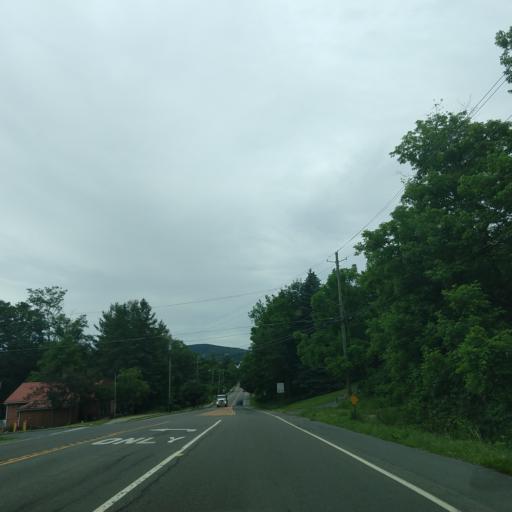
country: US
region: New York
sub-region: Tompkins County
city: Dryden
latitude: 42.4900
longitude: -76.3141
